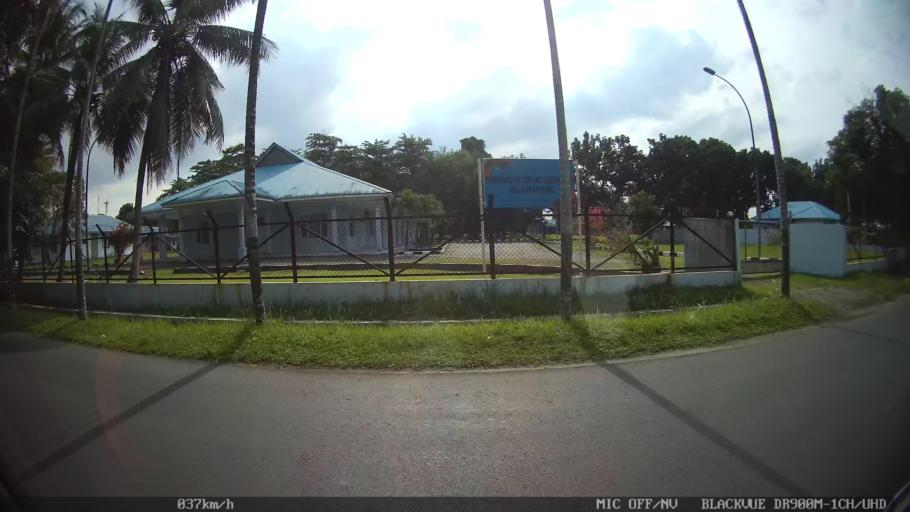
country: ID
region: North Sumatra
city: Medan
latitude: 3.5627
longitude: 98.6835
